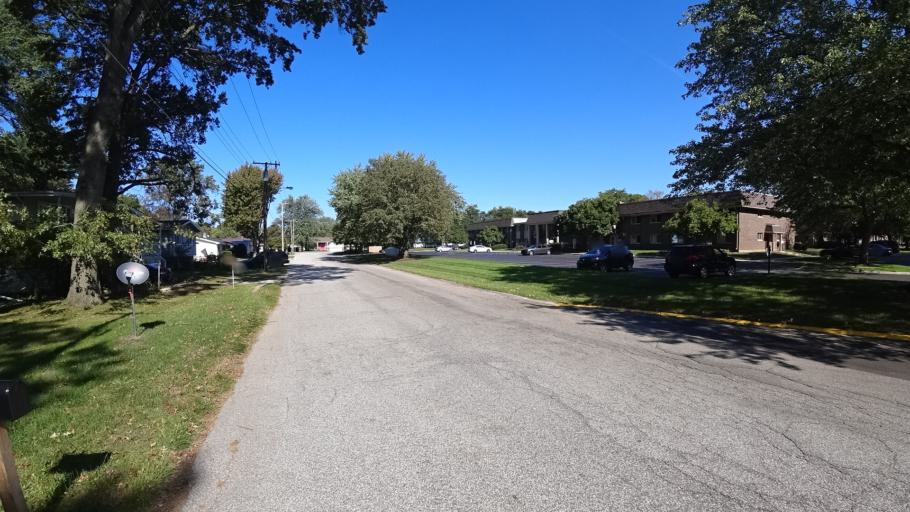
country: US
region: Indiana
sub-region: LaPorte County
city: Michigan City
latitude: 41.6864
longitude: -86.8904
